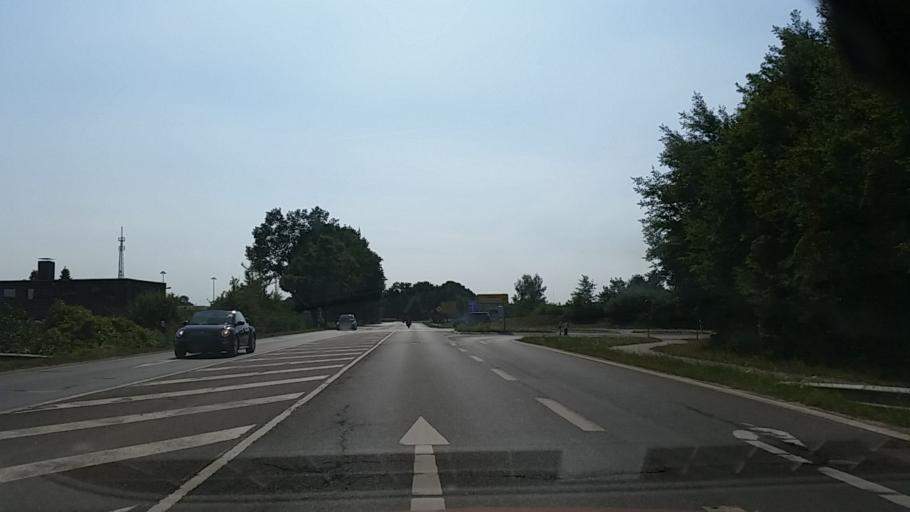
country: DE
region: Schleswig-Holstein
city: Reinbek
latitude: 53.5482
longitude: 10.2361
